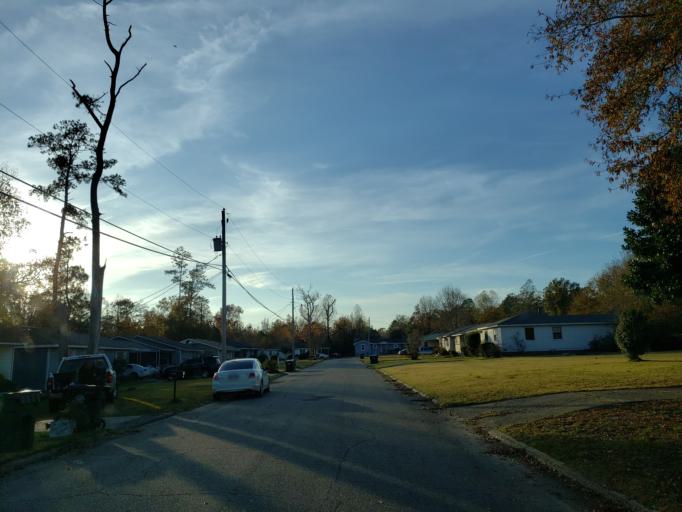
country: US
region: Mississippi
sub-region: Forrest County
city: Hattiesburg
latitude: 31.3292
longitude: -89.3124
